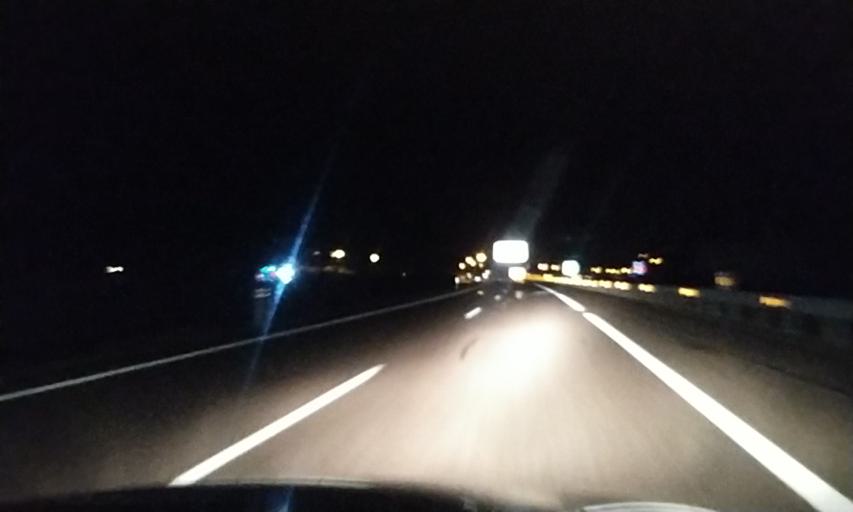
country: ES
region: Castille and Leon
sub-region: Provincia de Salamanca
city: Ciudad Rodrigo
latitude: 40.6188
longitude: -6.5113
